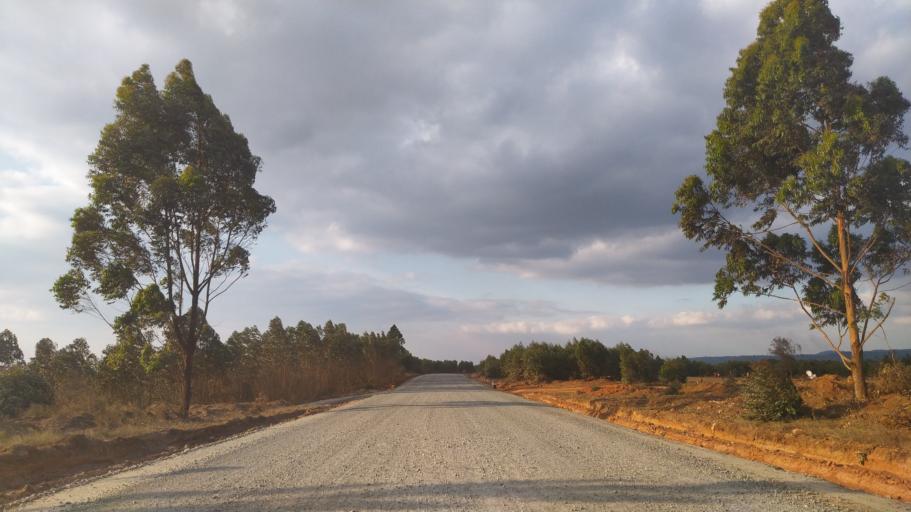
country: MG
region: Analamanga
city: Anjozorobe
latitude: -18.5211
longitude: 48.2624
